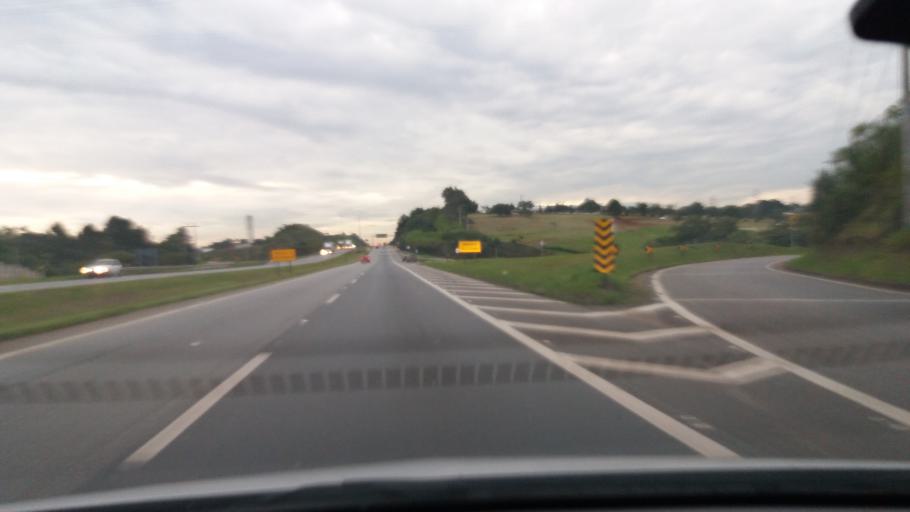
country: BR
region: Sao Paulo
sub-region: Atibaia
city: Atibaia
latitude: -23.0984
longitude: -46.5479
